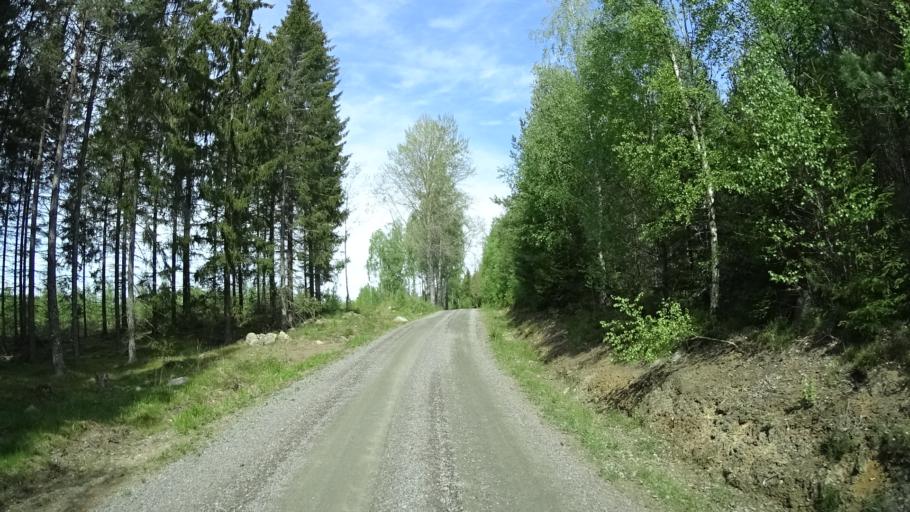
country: SE
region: OEstergoetland
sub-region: Finspangs Kommun
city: Finspang
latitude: 58.7841
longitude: 15.8784
